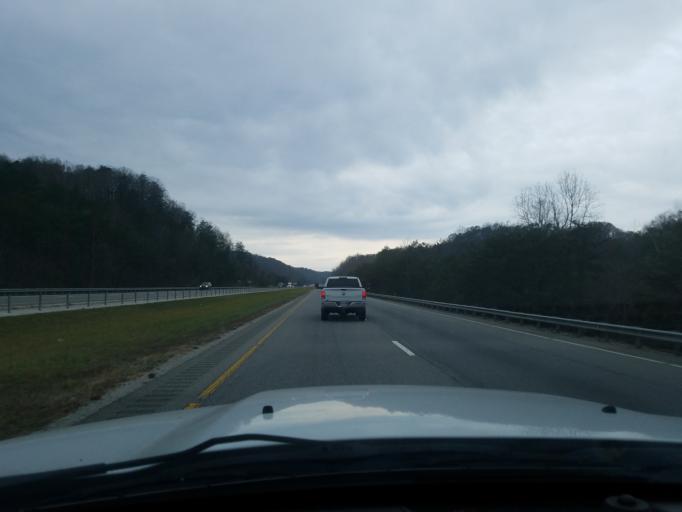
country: US
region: Kentucky
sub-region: Boyd County
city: Meads
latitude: 38.3654
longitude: -82.7807
